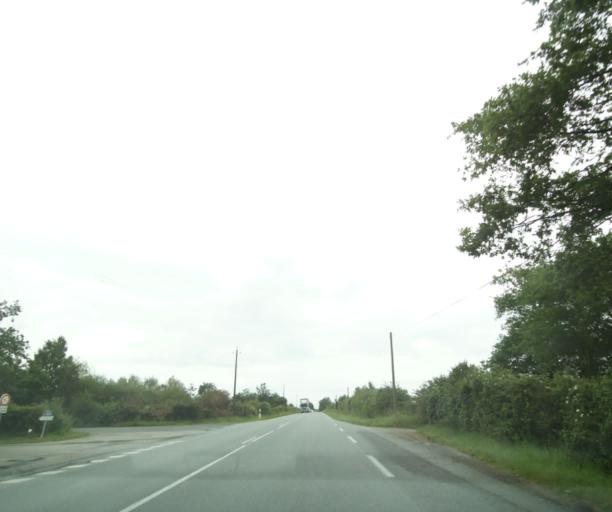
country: FR
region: Poitou-Charentes
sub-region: Departement des Deux-Sevres
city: Viennay
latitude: 46.6978
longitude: -0.2413
